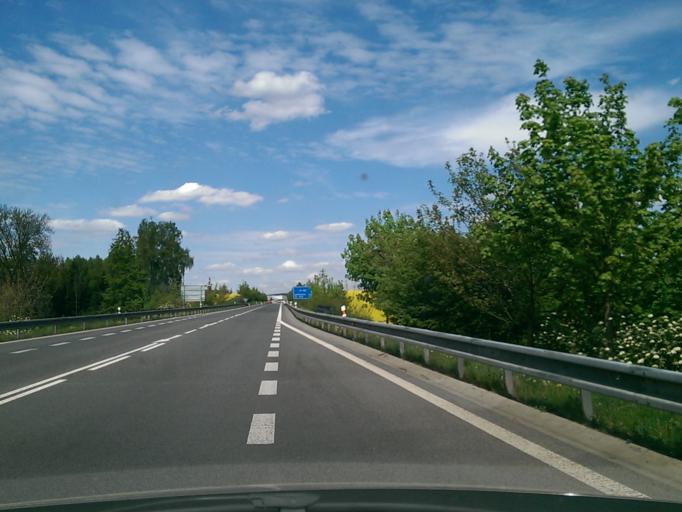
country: CZ
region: Liberecky
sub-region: Okres Semily
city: Turnov
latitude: 50.5948
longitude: 15.1426
